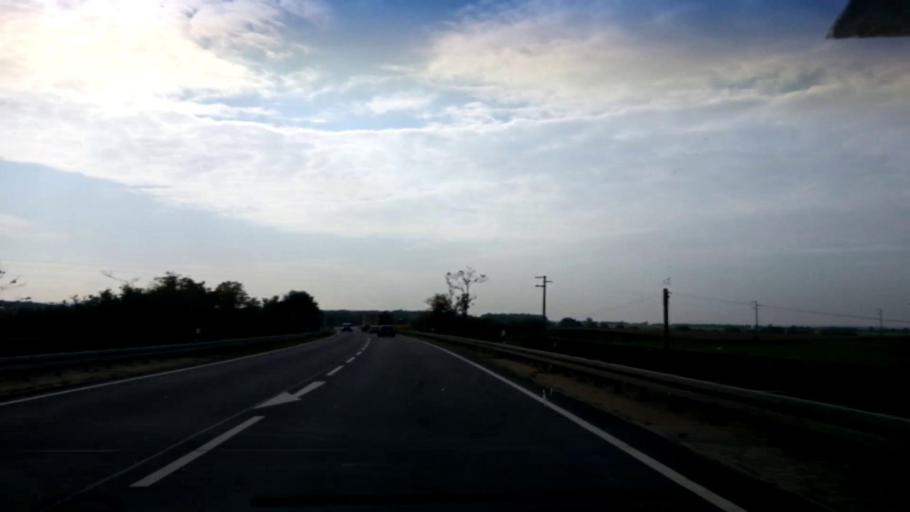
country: DE
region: Bavaria
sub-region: Regierungsbezirk Unterfranken
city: Prichsenstadt
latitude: 49.8436
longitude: 10.3509
